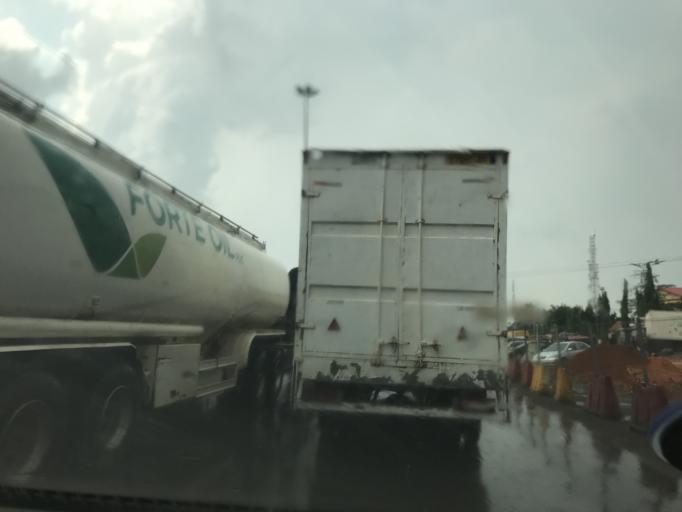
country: NG
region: Lagos
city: Oshodi
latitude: 6.5534
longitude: 3.3461
